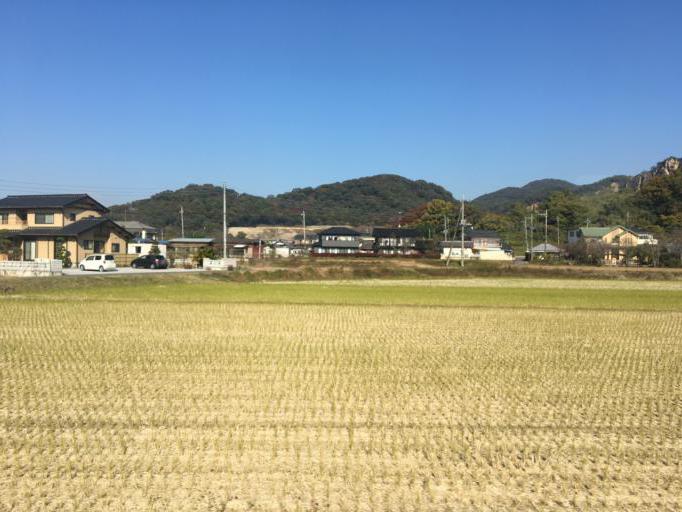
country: JP
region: Tochigi
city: Sano
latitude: 36.3268
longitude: 139.6498
